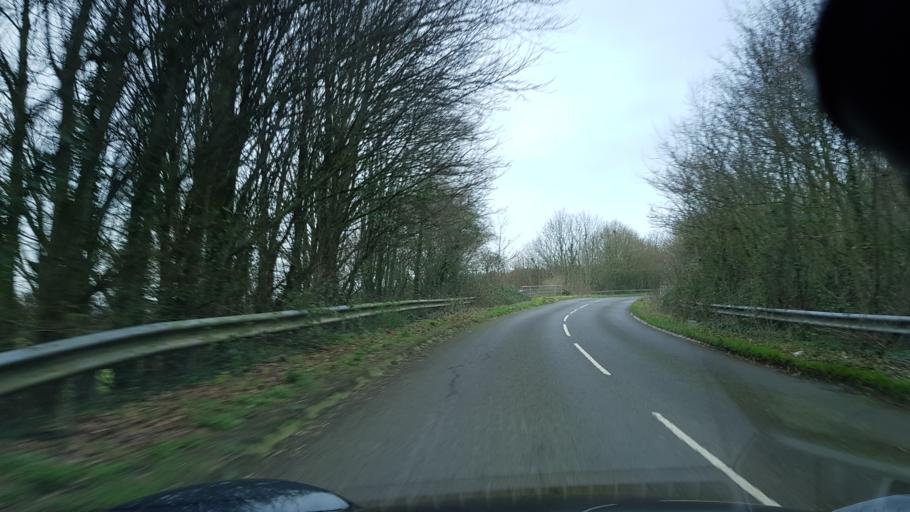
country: GB
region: England
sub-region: Somerset
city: Taunton
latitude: 51.0062
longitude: -3.0695
